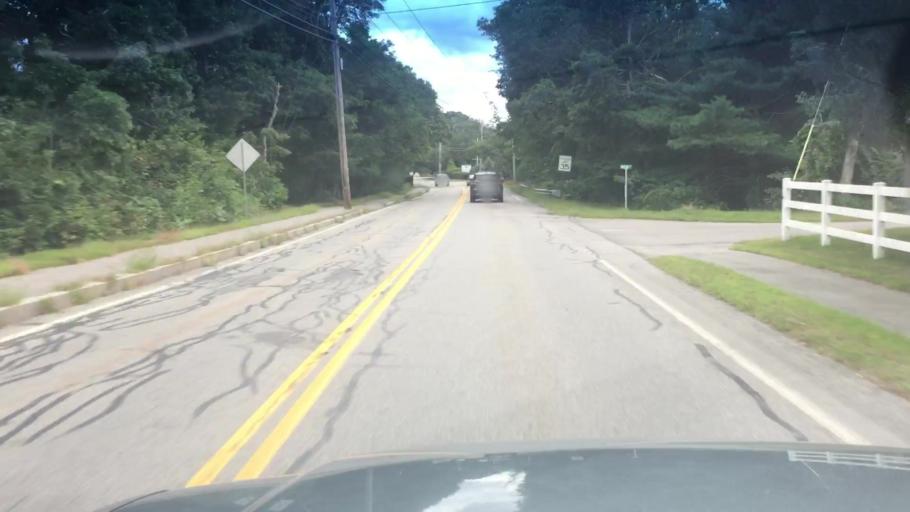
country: US
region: Massachusetts
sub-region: Barnstable County
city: Pocasset
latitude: 41.6963
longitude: -70.5983
